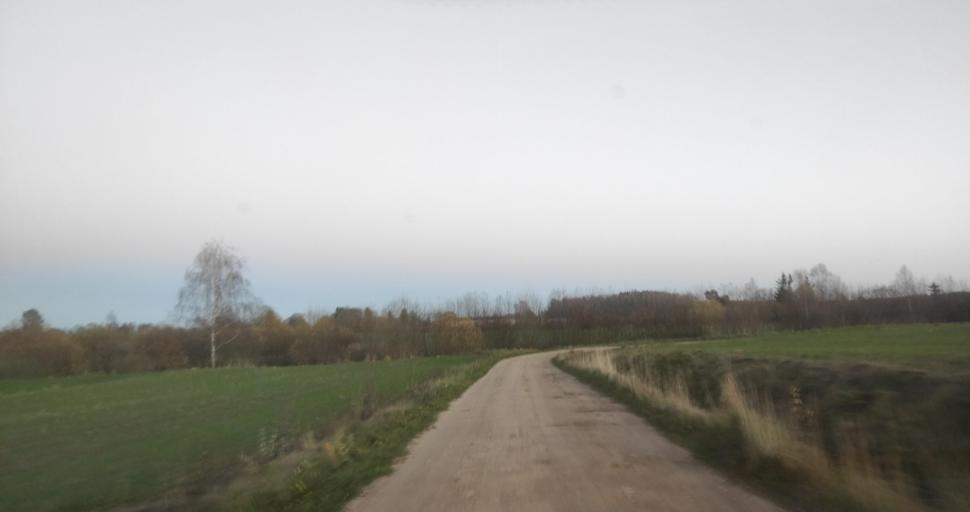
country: LV
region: Saldus Rajons
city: Saldus
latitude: 56.8046
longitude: 22.2749
